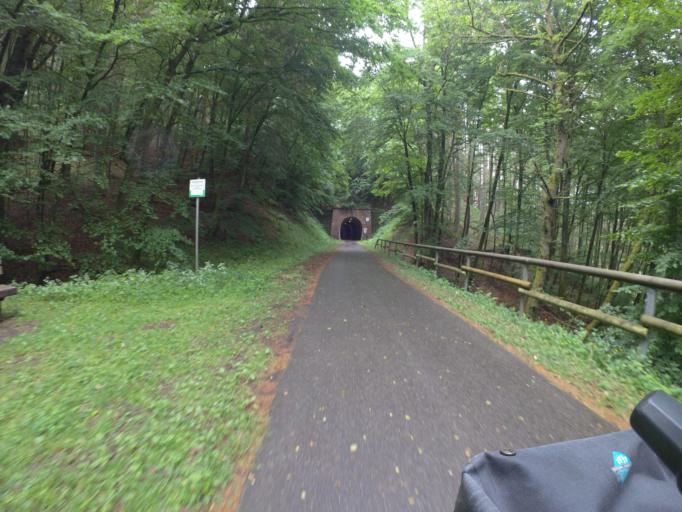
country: DE
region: Rheinland-Pfalz
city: Plein
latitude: 50.0203
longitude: 6.8758
